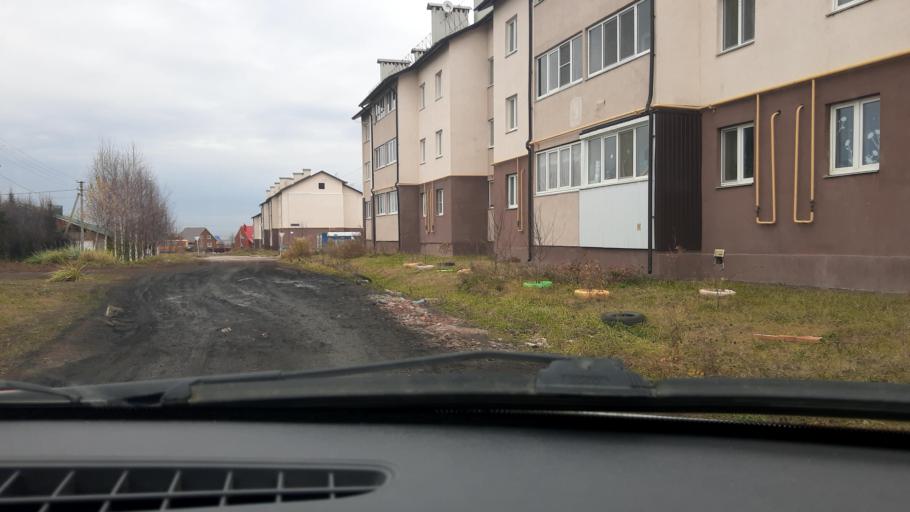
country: RU
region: Bashkortostan
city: Avdon
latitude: 54.6963
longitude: 55.8026
